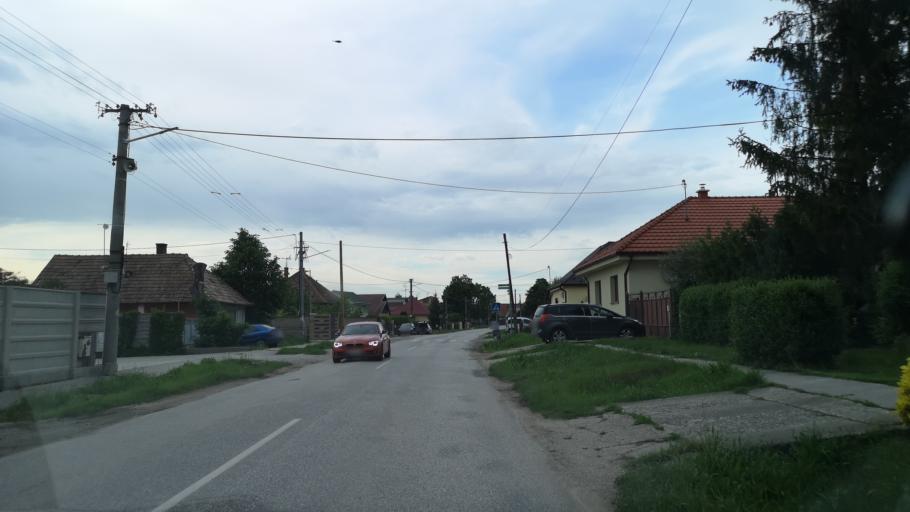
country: SK
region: Nitriansky
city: Sellye
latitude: 48.2380
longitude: 17.9177
